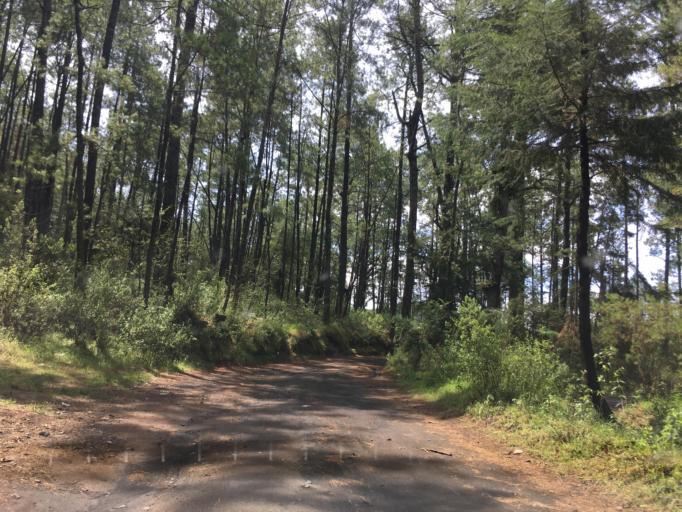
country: MX
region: Michoacan
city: Angahuan
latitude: 19.5151
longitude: -102.2191
